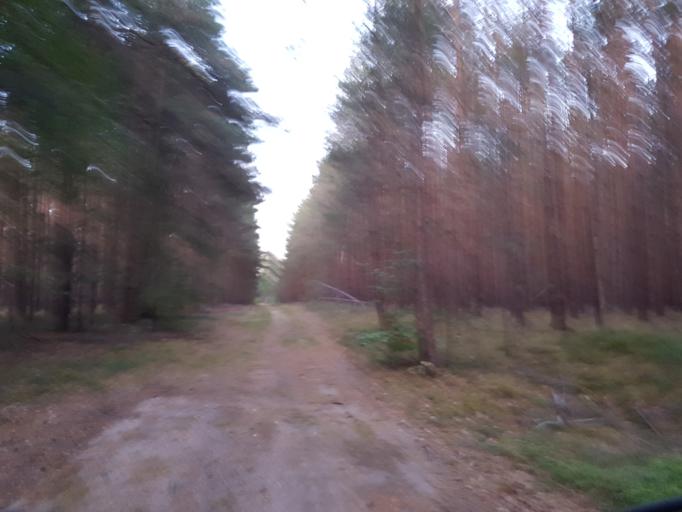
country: DE
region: Brandenburg
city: Trobitz
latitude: 51.5555
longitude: 13.4283
